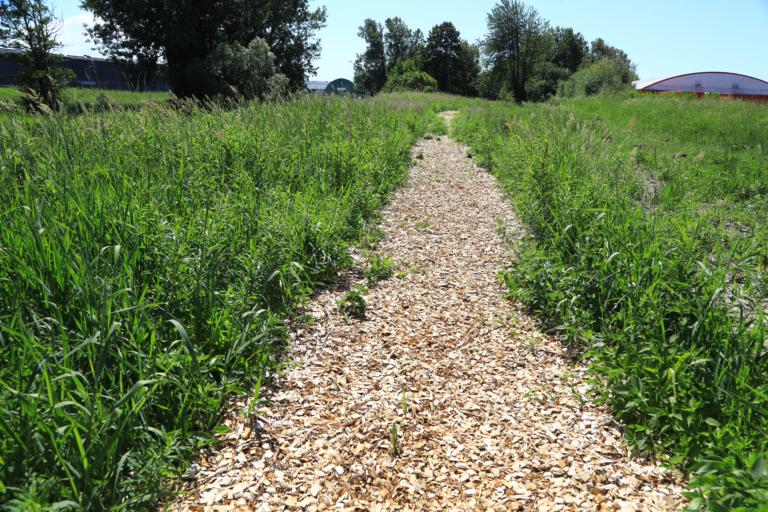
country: SE
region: Halland
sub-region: Kungsbacka Kommun
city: Kungsbacka
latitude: 57.5042
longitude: 12.0740
